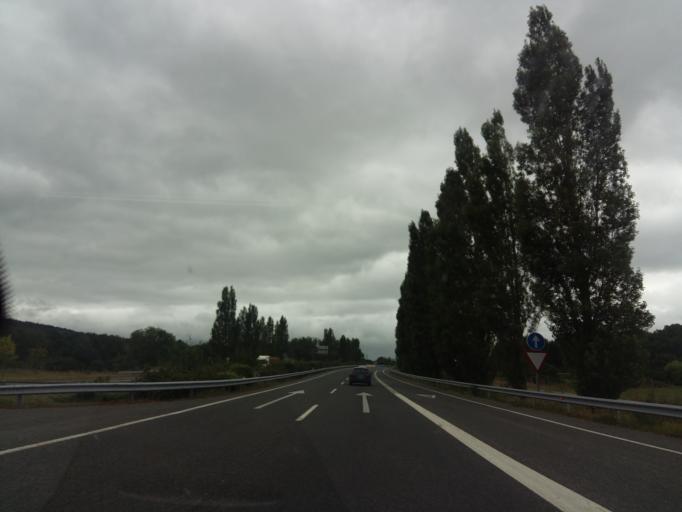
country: ES
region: Navarre
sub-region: Provincia de Navarra
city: Arruazu
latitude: 42.9228
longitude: -2.0040
